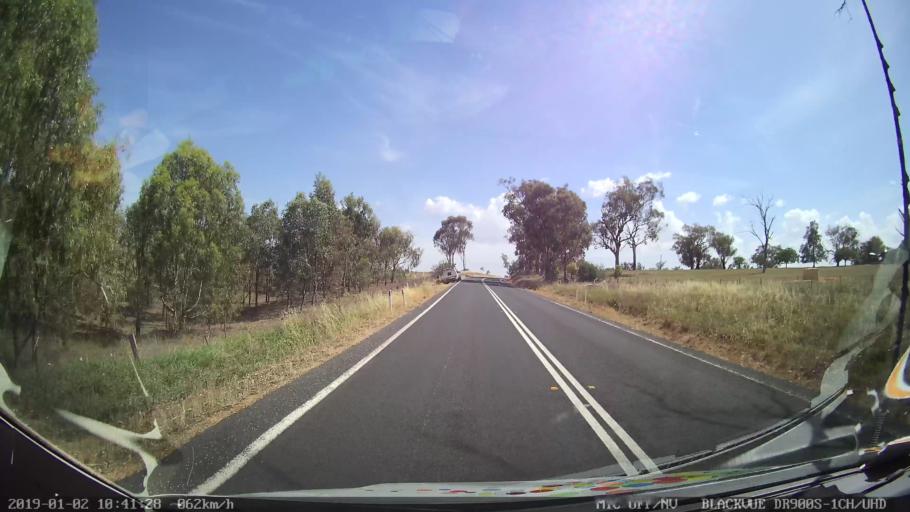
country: AU
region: New South Wales
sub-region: Cootamundra
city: Cootamundra
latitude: -34.7938
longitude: 148.3065
